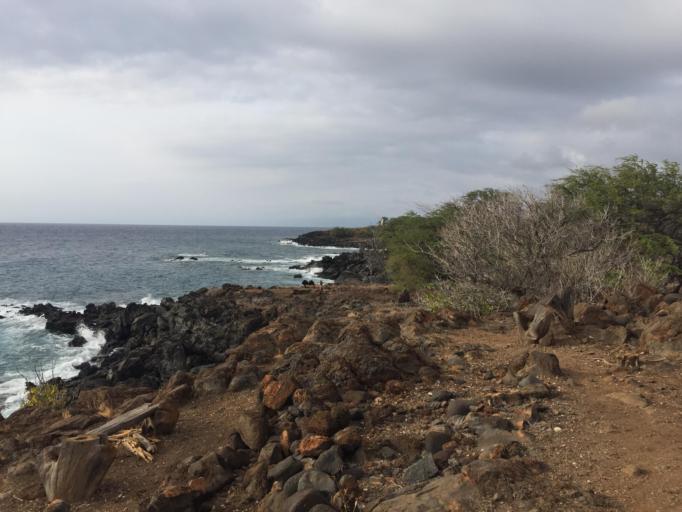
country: US
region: Hawaii
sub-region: Hawaii County
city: Hawi
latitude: 20.1767
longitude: -155.8999
